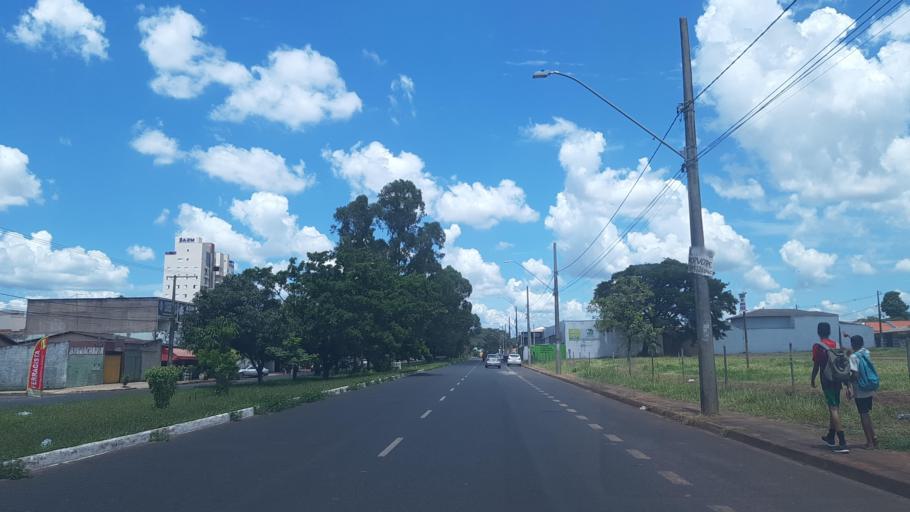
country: BR
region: Minas Gerais
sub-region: Uberlandia
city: Uberlandia
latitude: -18.9503
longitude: -48.3214
